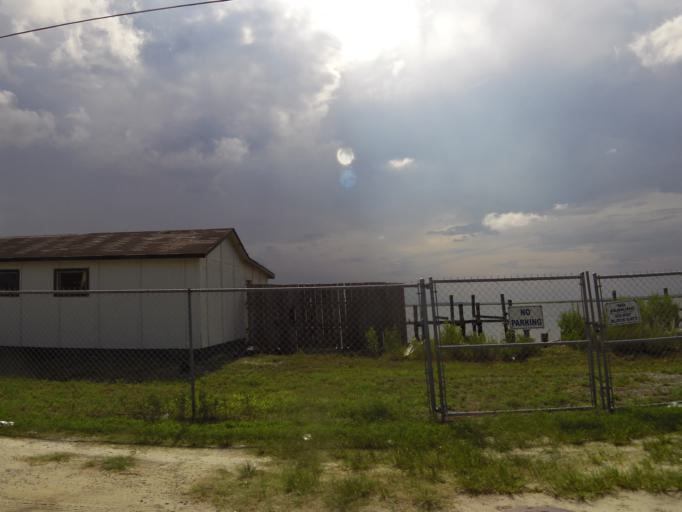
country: US
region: Florida
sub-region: Nassau County
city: Fernandina Beach
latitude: 30.6733
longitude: -81.4646
